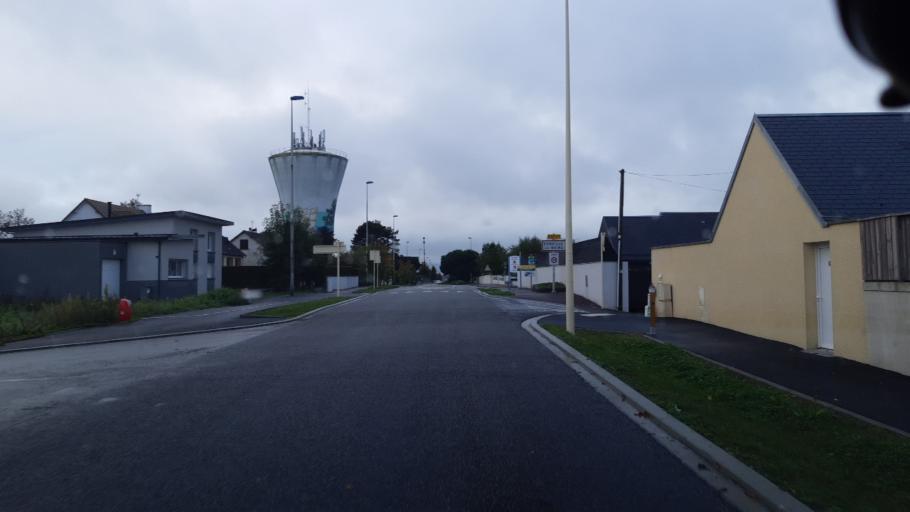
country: FR
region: Lower Normandy
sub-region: Departement de la Manche
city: Donville-les-Bains
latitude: 48.8550
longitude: -1.5631
